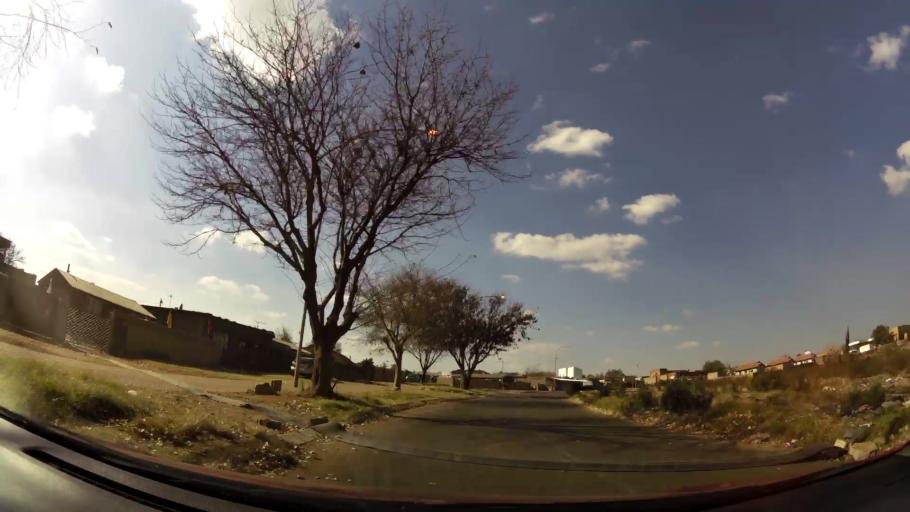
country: ZA
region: Gauteng
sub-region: City of Johannesburg Metropolitan Municipality
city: Roodepoort
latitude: -26.2132
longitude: 27.8845
